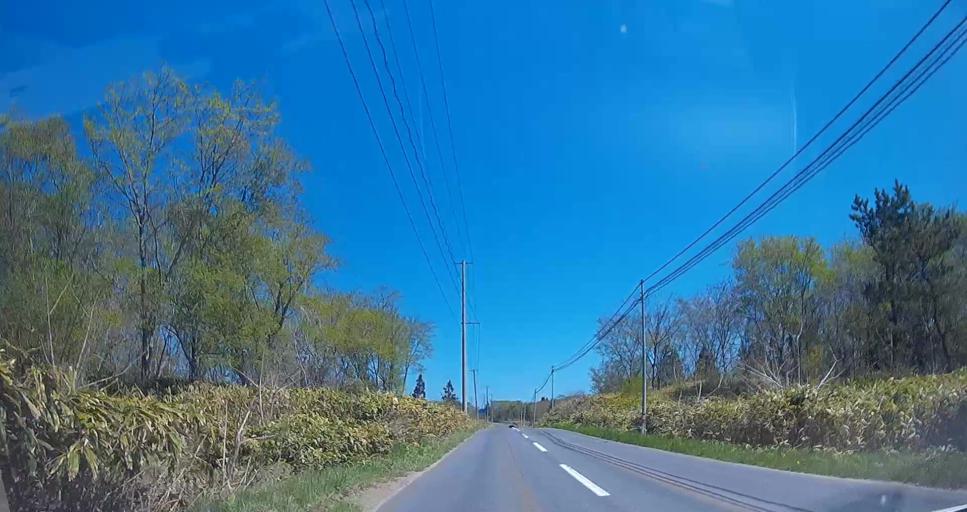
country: JP
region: Aomori
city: Misawa
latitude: 40.9176
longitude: 141.3763
